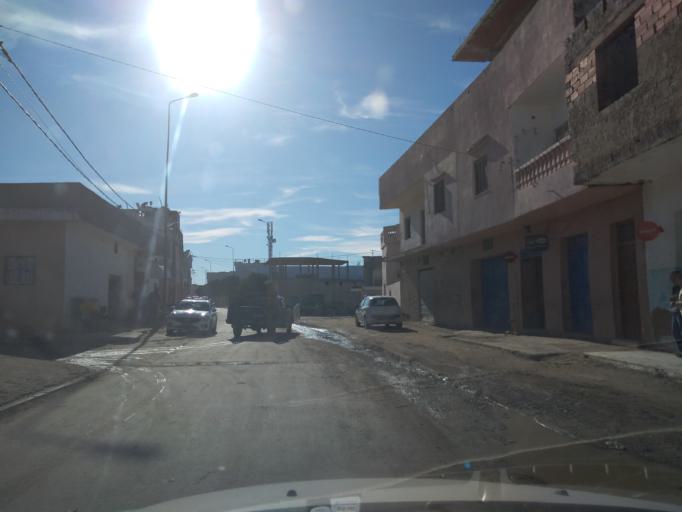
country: TN
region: Ariana
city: Qal'at al Andalus
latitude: 37.0665
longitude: 10.1212
